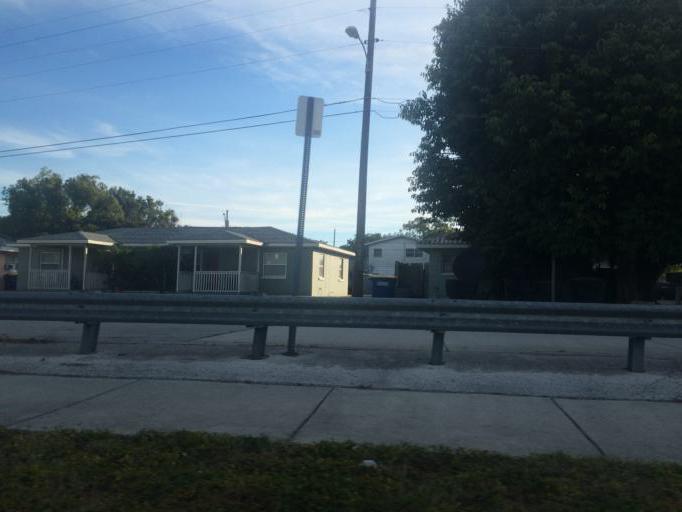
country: US
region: Florida
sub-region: Pinellas County
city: Clearwater
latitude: 27.9618
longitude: -82.7630
